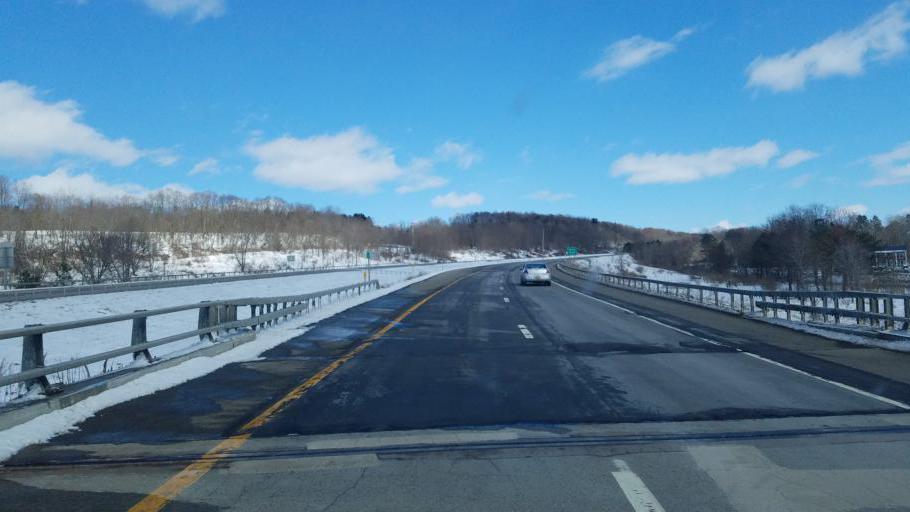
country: US
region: New York
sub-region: Chautauqua County
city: Falconer
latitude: 42.1359
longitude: -79.1803
